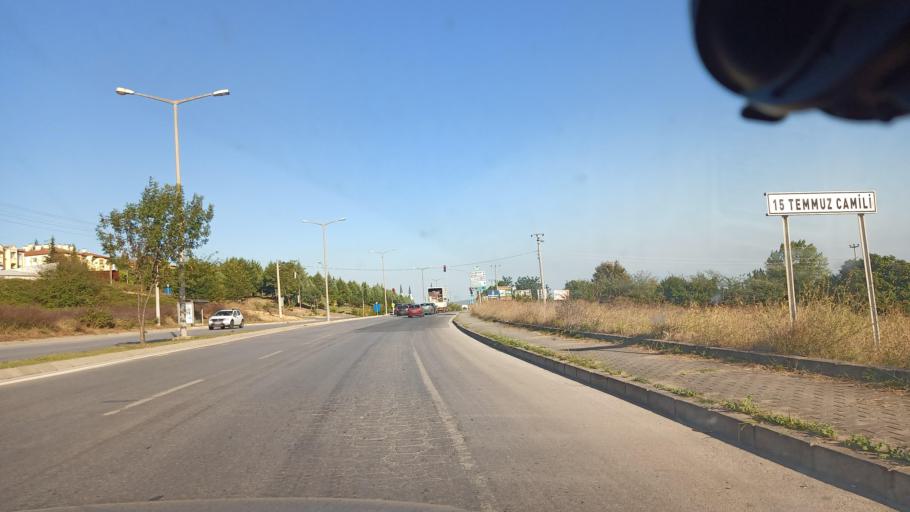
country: TR
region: Sakarya
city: Kazimpasa
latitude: 40.8530
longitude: 30.3059
